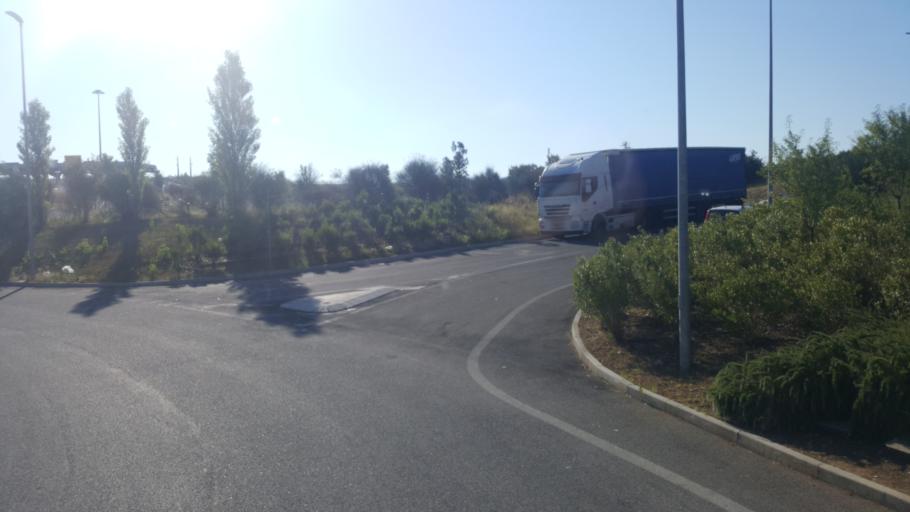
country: IT
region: Latium
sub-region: Citta metropolitana di Roma Capitale
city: Albuccione
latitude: 41.9685
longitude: 12.6892
